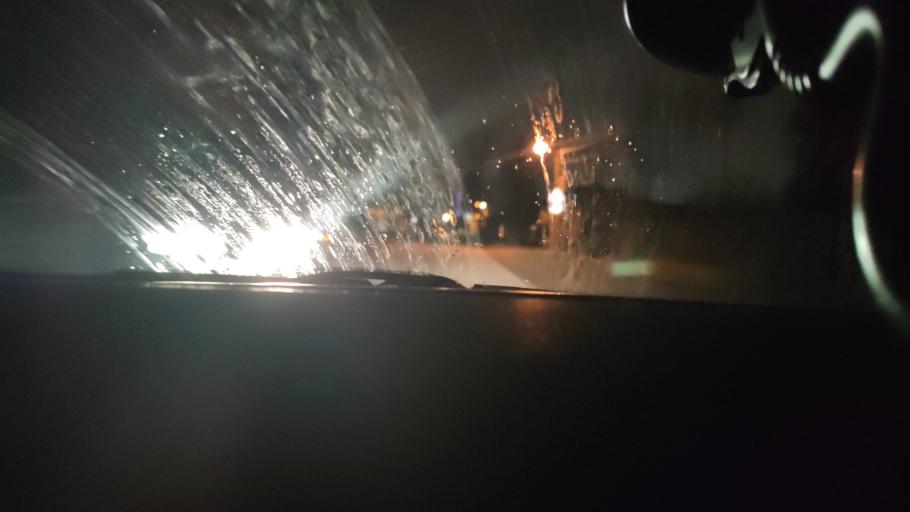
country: RU
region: Perm
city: Perm
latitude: 58.0443
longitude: 56.3284
